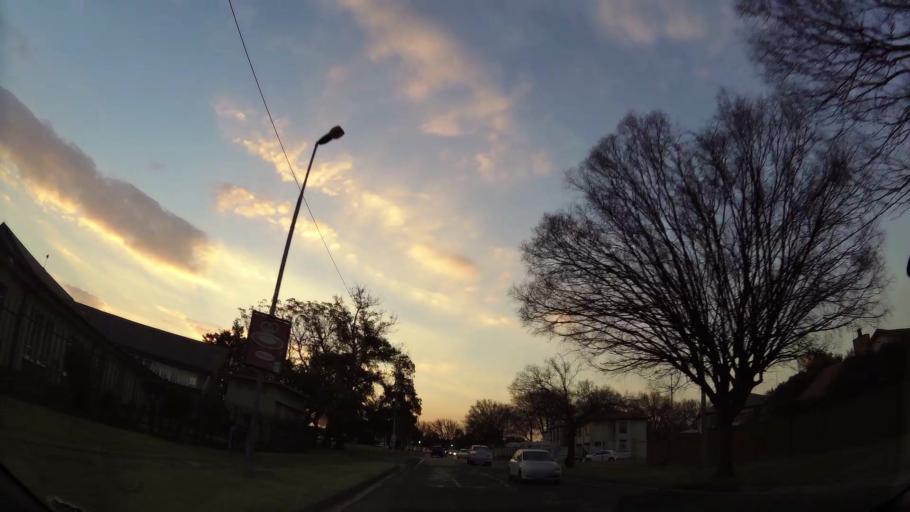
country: ZA
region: Gauteng
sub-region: Ekurhuleni Metropolitan Municipality
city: Benoni
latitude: -26.1655
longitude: 28.3133
